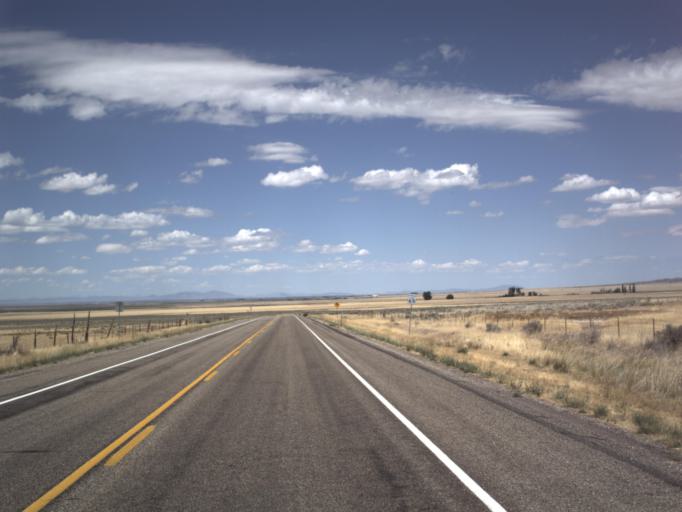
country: US
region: Utah
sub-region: Millard County
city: Fillmore
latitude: 39.1095
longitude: -112.2715
